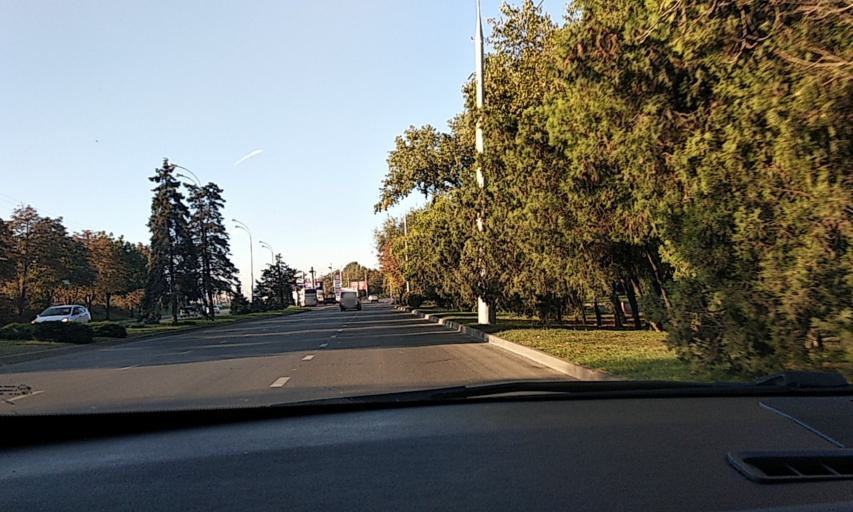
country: RU
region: Adygeya
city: Yablonovskiy
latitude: 45.0089
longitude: 38.9695
